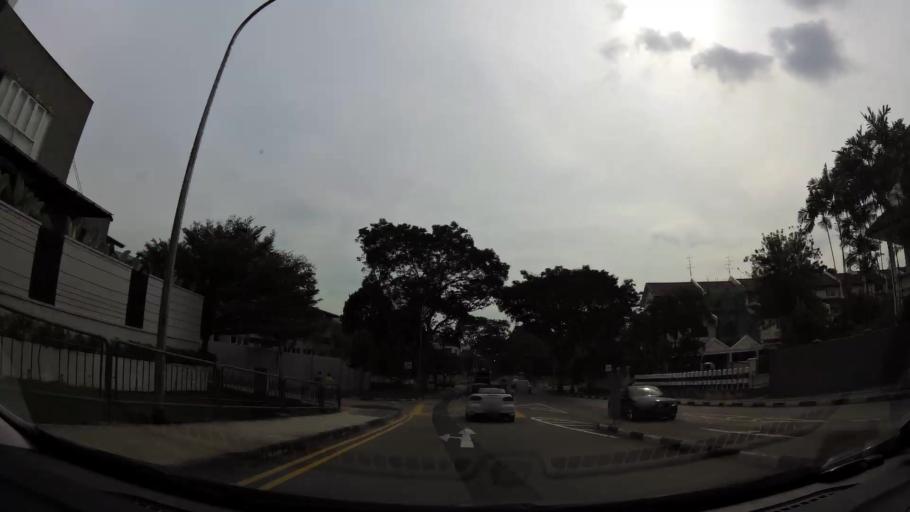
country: SG
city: Singapore
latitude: 1.3256
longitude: 103.7930
